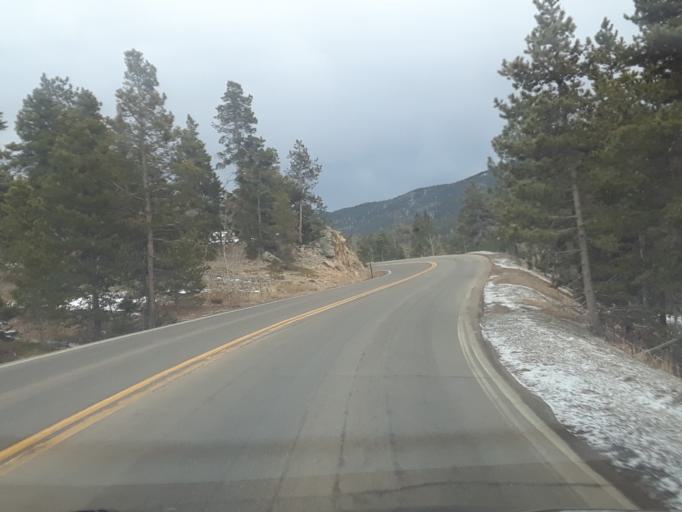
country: US
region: Colorado
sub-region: Gilpin County
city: Central City
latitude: 39.8402
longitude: -105.4625
